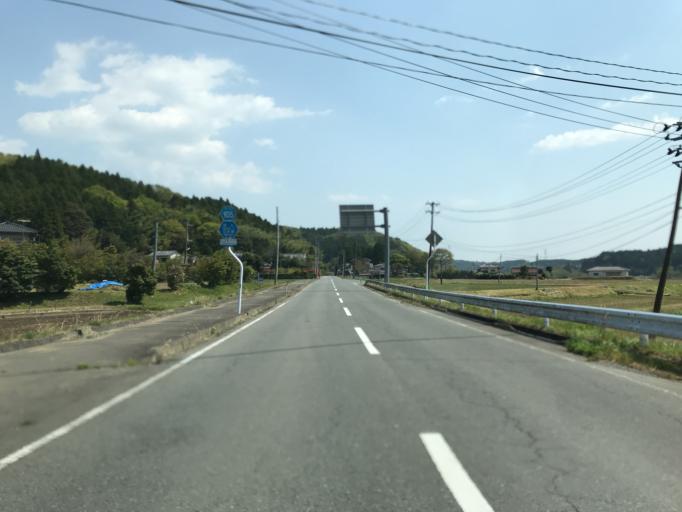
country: JP
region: Ibaraki
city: Kitaibaraki
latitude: 36.9365
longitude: 140.7329
